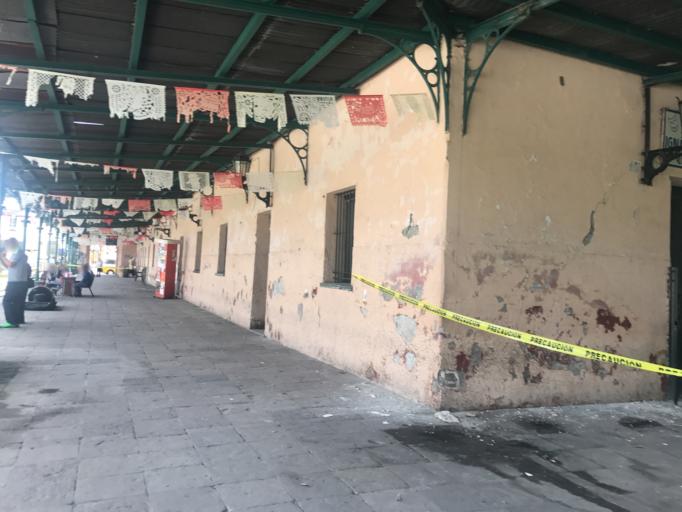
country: MX
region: Morelos
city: Cuautla Morelos
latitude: 18.8165
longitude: -98.9542
